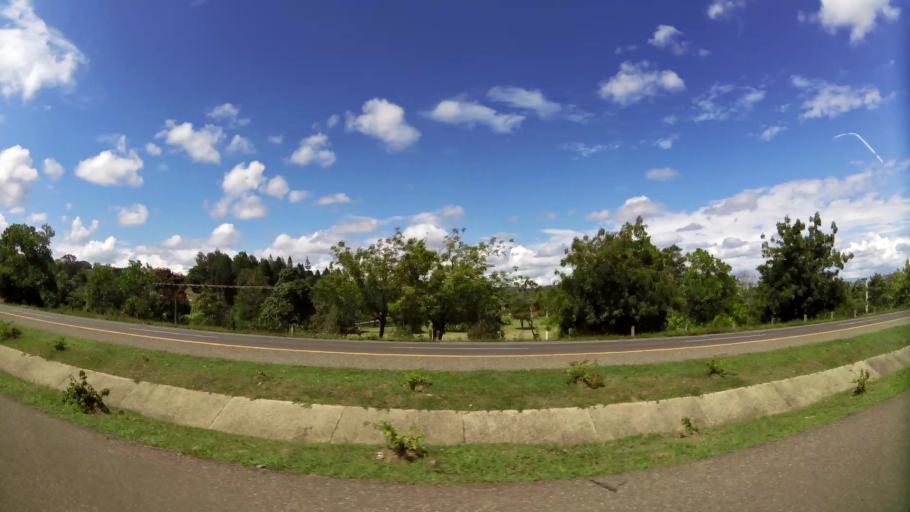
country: DO
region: La Vega
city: Concepcion de La Vega
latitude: 19.2497
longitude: -70.5533
